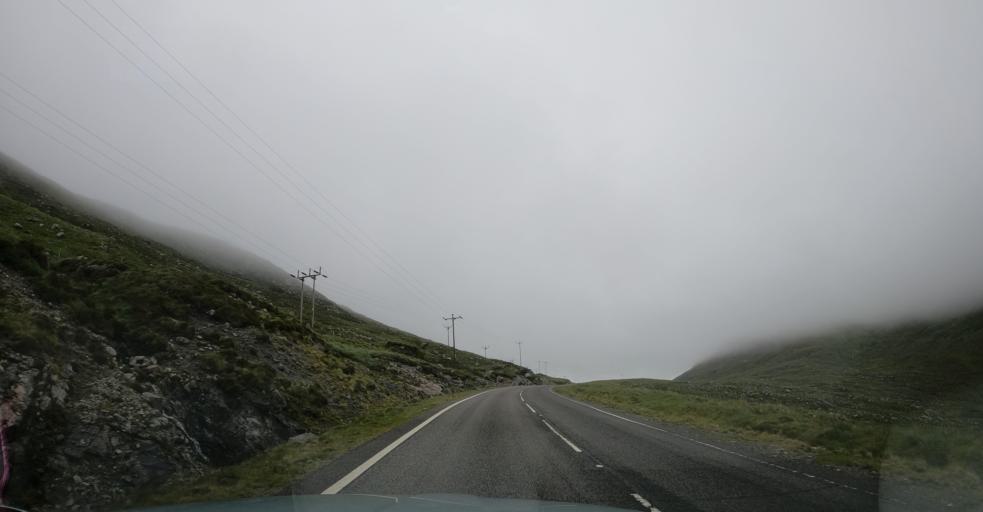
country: GB
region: Scotland
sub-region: Eilean Siar
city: Harris
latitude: 57.9449
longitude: -6.8114
